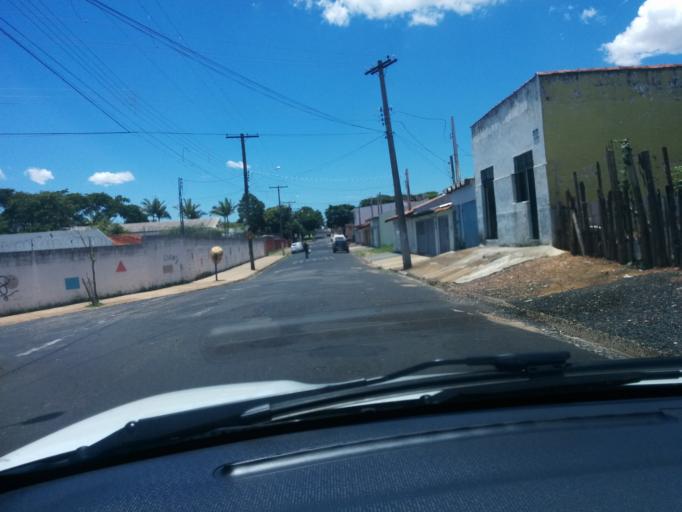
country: BR
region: Sao Paulo
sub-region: Franca
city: Franca
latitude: -20.5751
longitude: -47.3722
